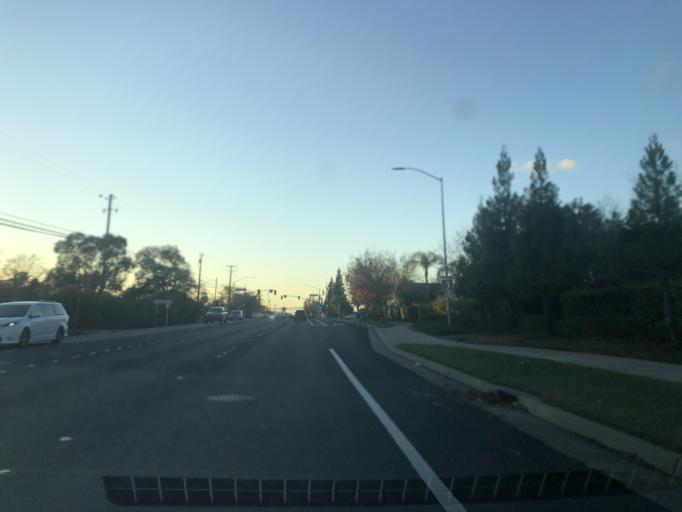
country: US
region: California
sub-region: Sacramento County
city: Antelope
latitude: 38.7520
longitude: -121.3349
